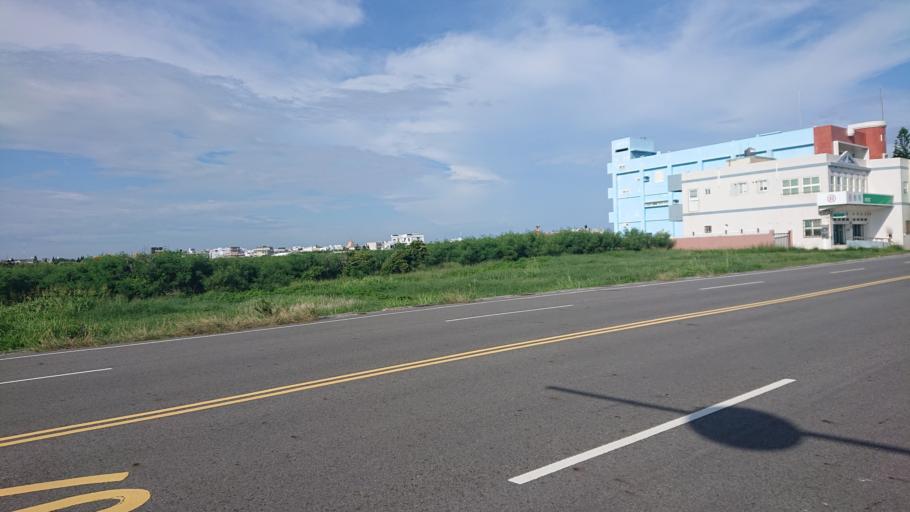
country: TW
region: Taiwan
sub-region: Penghu
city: Ma-kung
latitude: 23.5252
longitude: 119.5962
